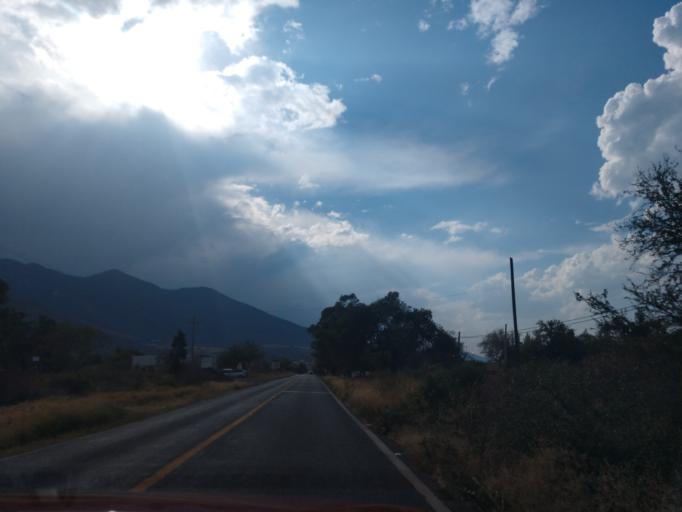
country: MX
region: Jalisco
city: San Juan Cosala
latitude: 20.1938
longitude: -103.2916
